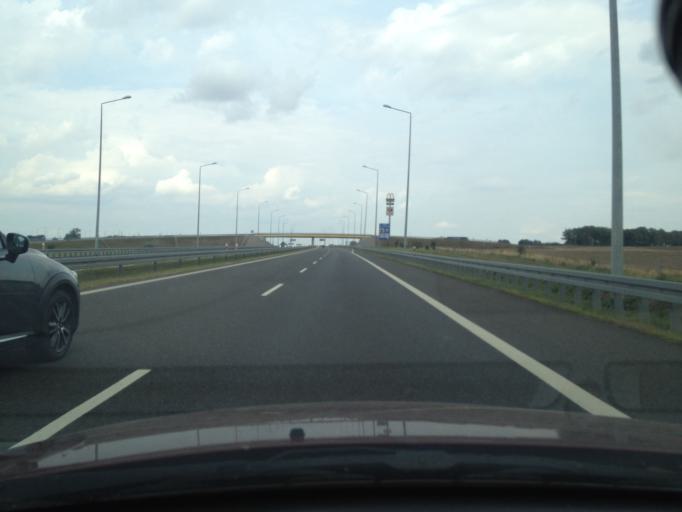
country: PL
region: West Pomeranian Voivodeship
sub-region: Powiat pyrzycki
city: Kozielice
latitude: 53.0464
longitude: 14.8661
